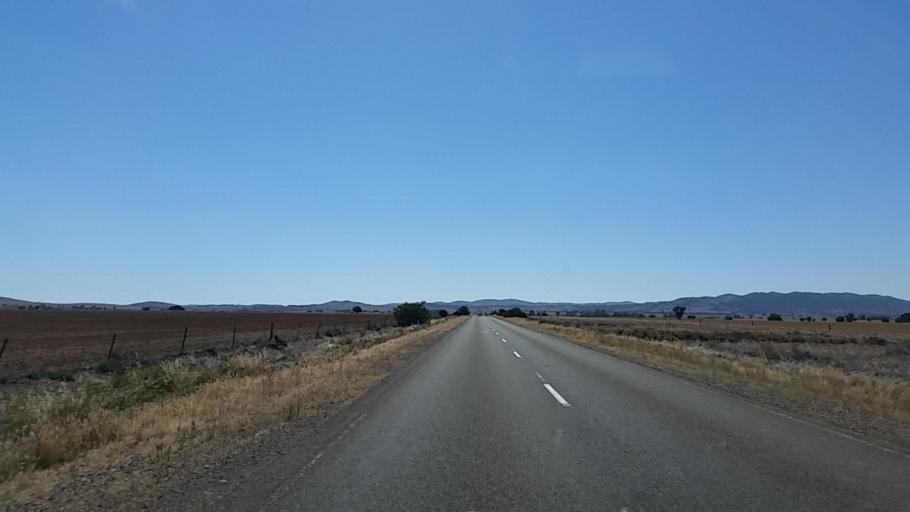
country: AU
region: South Australia
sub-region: Peterborough
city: Peterborough
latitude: -32.6543
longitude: 138.6028
